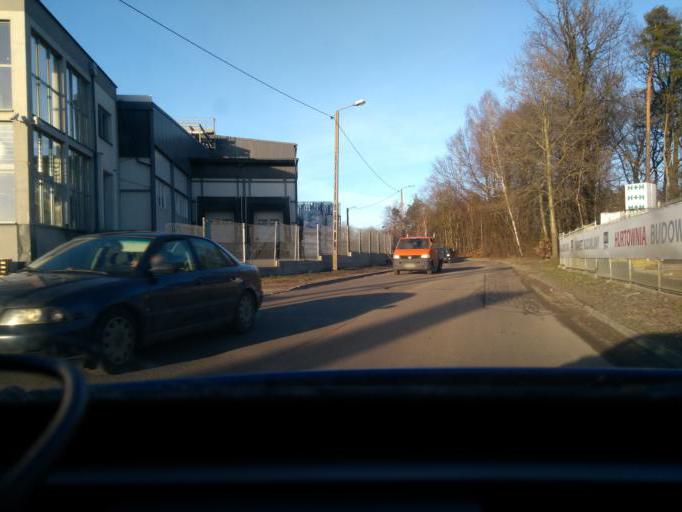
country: PL
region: Pomeranian Voivodeship
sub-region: Powiat kartuski
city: Kartuzy
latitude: 54.3326
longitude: 18.2075
